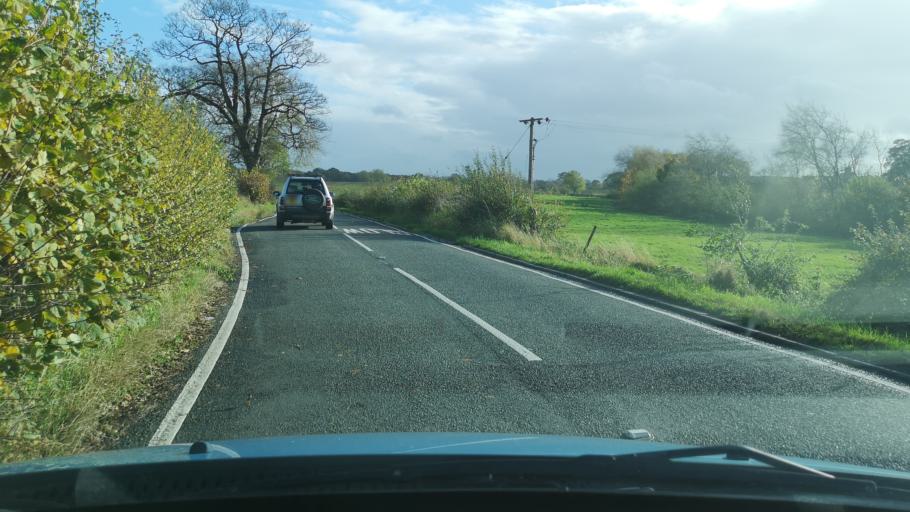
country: GB
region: England
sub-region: City and Borough of Wakefield
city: Crofton
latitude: 53.6447
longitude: -1.4214
